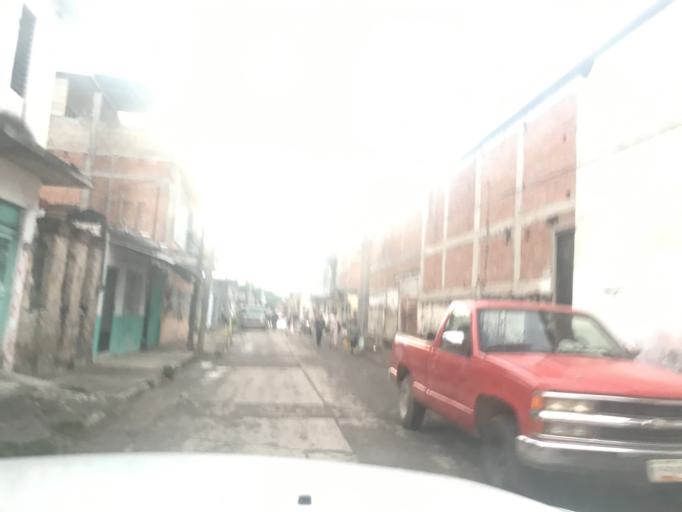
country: MX
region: Morelos
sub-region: Jojutla
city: Jojutla
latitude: 18.6129
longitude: -99.1793
